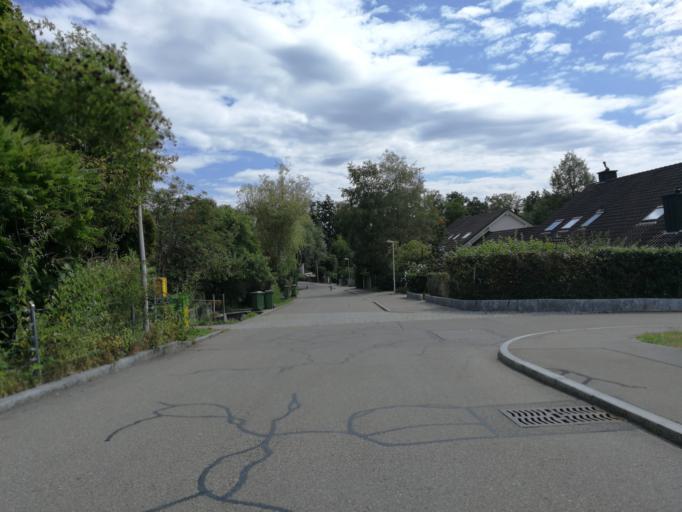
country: CH
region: Zurich
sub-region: Bezirk Meilen
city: Feldmeilen
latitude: 47.2862
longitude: 8.6253
